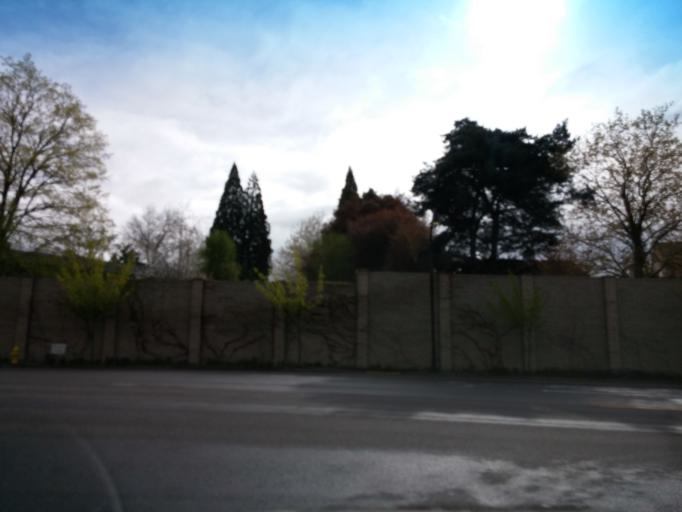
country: US
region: Oregon
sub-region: Washington County
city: Oak Hills
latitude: 45.5356
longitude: -122.8407
